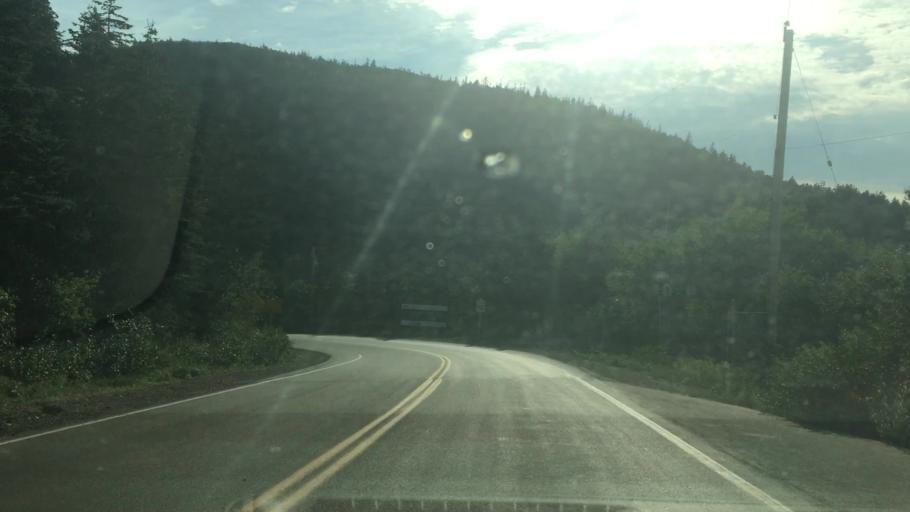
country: CA
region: Nova Scotia
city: Sydney Mines
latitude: 46.8227
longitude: -60.8262
